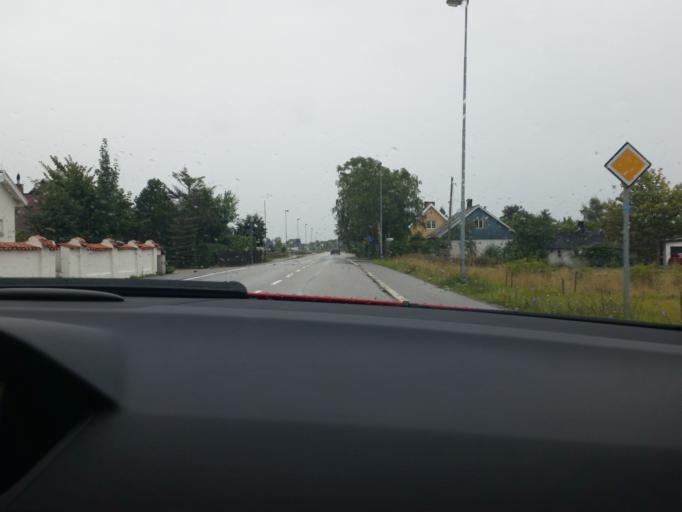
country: SE
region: Skane
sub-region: Malmo
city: Bunkeflostrand
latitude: 55.5461
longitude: 12.9182
